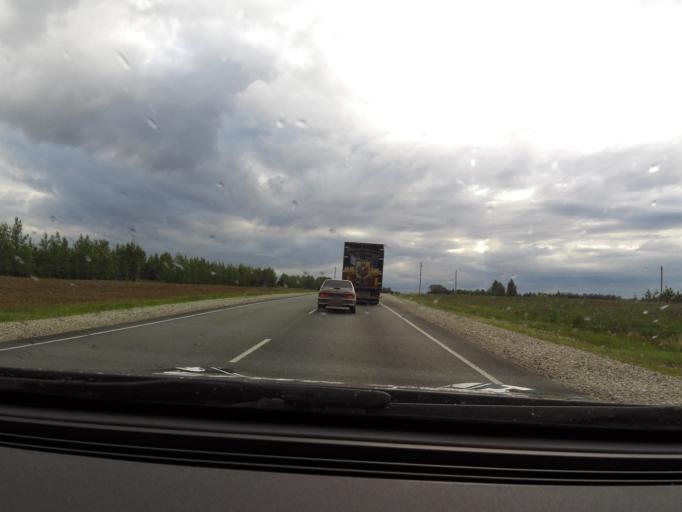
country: RU
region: Tatarstan
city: Nizhniye Vyazovyye
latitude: 55.7235
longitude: 48.4480
